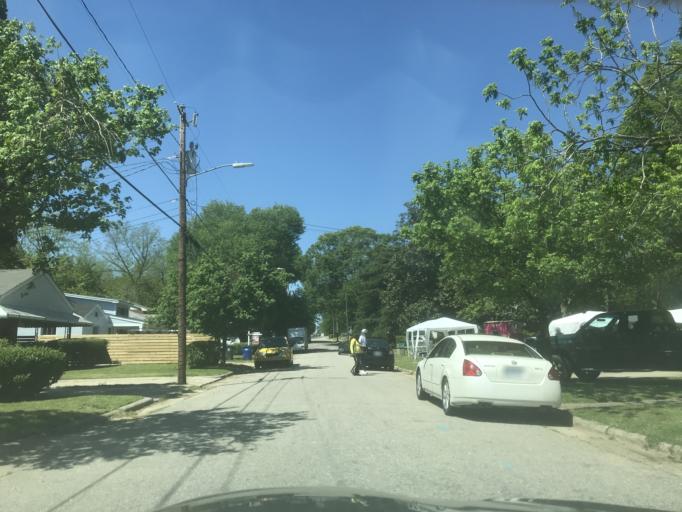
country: US
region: North Carolina
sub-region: Wake County
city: Raleigh
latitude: 35.7636
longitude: -78.6341
